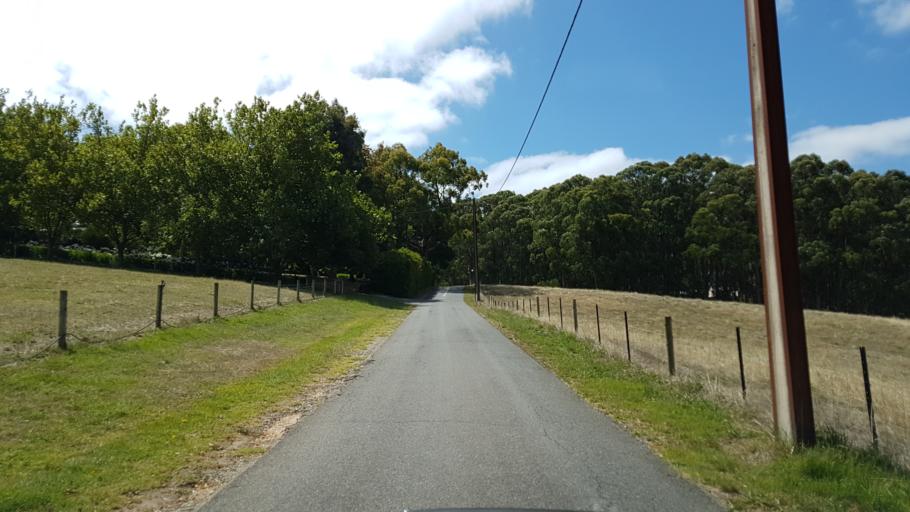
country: AU
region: South Australia
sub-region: Adelaide Hills
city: Crafers
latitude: -34.9737
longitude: 138.7176
